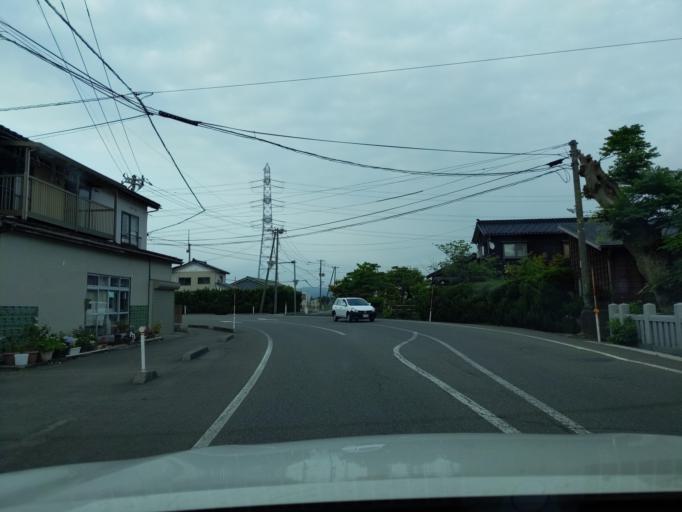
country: JP
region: Niigata
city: Kashiwazaki
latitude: 37.4080
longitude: 138.6064
